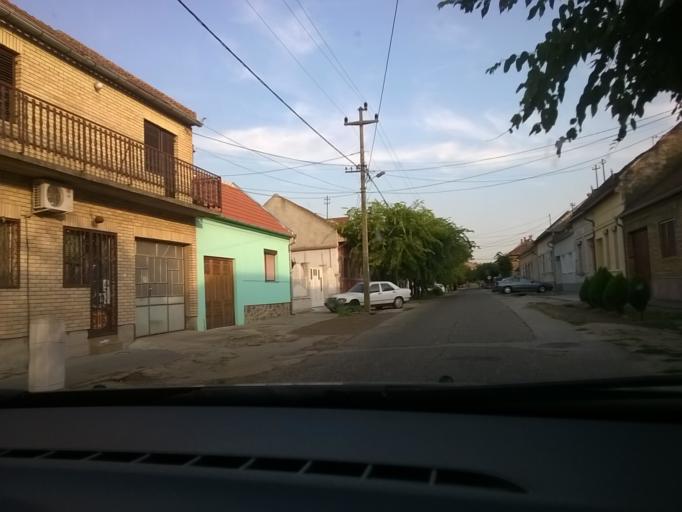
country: RS
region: Autonomna Pokrajina Vojvodina
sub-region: Juznobanatski Okrug
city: Vrsac
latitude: 45.1220
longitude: 21.2899
